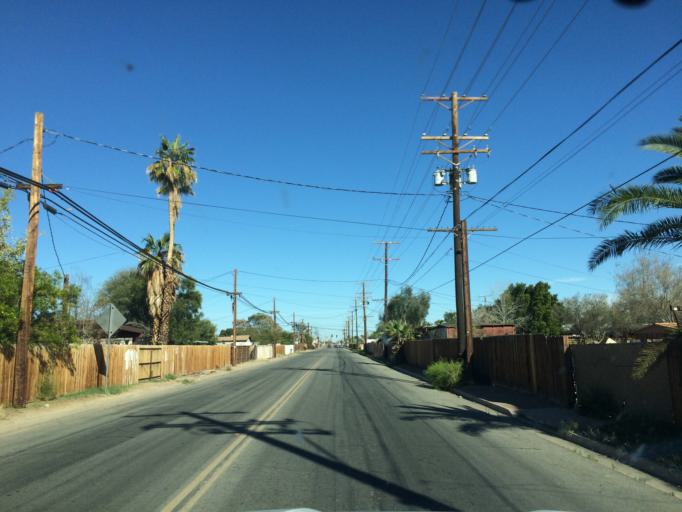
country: US
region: California
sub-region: Imperial County
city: El Centro
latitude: 32.7815
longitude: -115.5562
